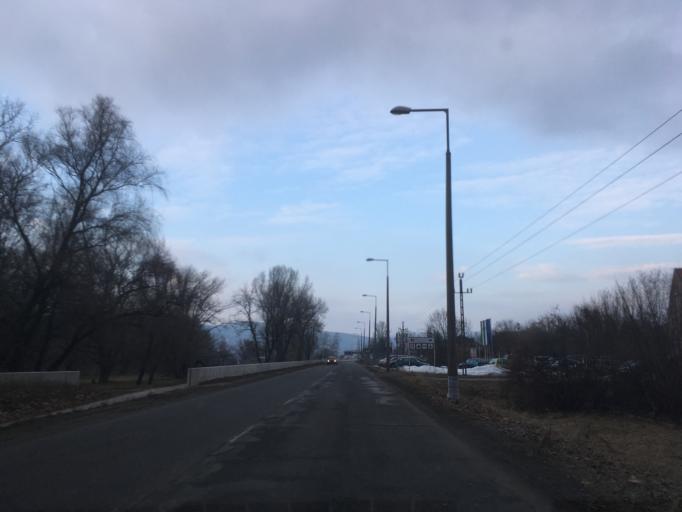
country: HU
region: Pest
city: Visegrad
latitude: 47.7818
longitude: 18.9671
